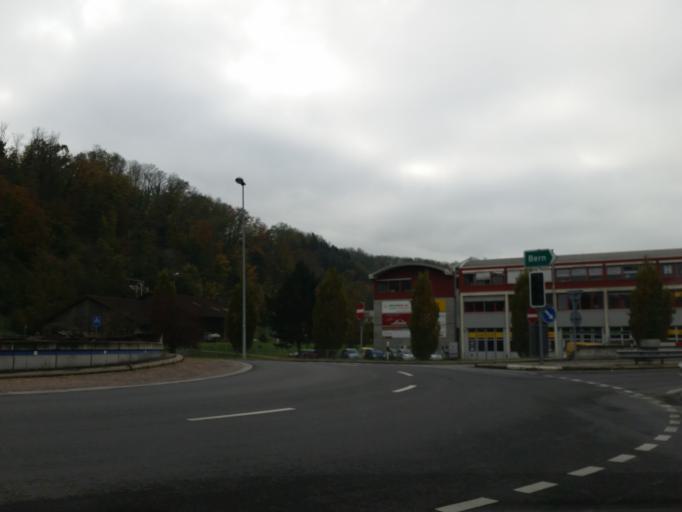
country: CH
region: Vaud
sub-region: Jura-Nord vaudois District
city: Yverdon-les-Bains
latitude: 46.7615
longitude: 6.6457
